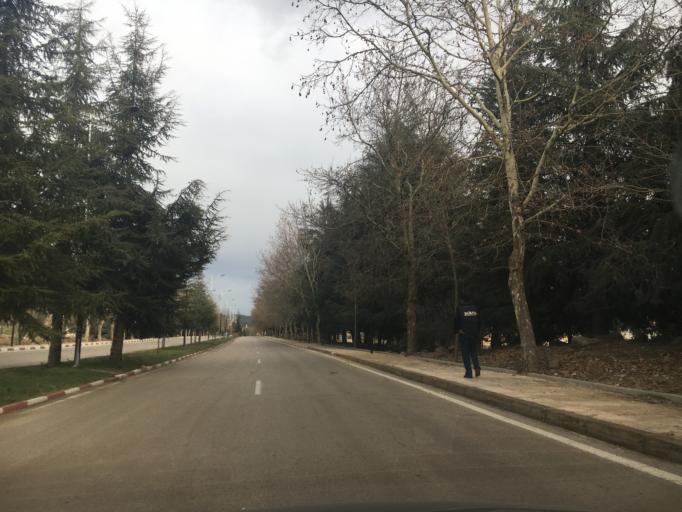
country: MA
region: Meknes-Tafilalet
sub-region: Ifrane
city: Ifrane
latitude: 33.5284
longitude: -5.1293
